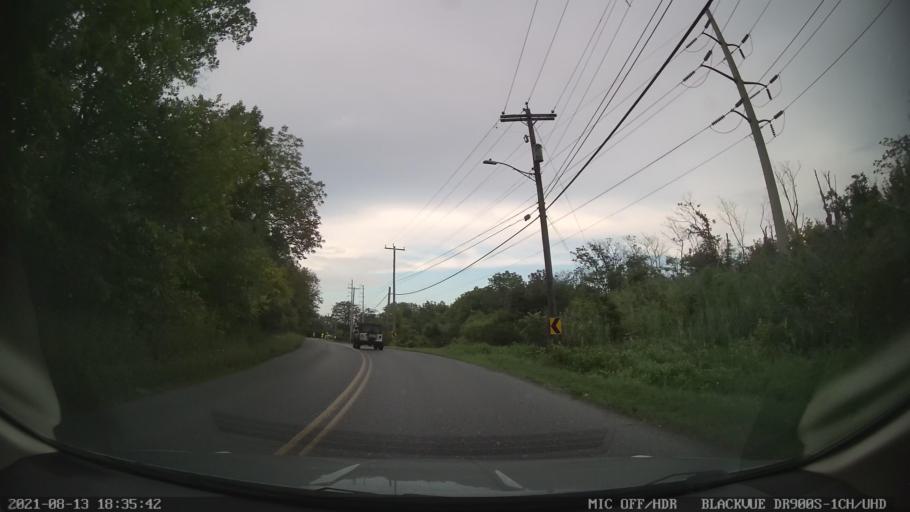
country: US
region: Pennsylvania
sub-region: Lehigh County
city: Stiles
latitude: 40.6709
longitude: -75.5096
